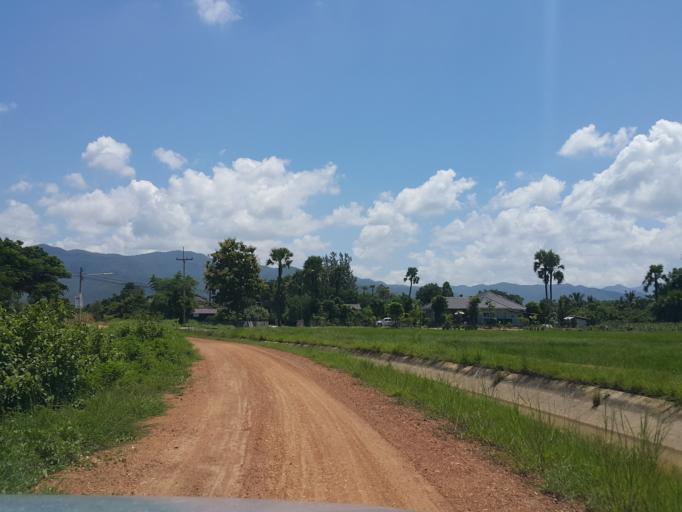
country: TH
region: Lamphun
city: Ban Thi
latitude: 18.6694
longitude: 99.1477
